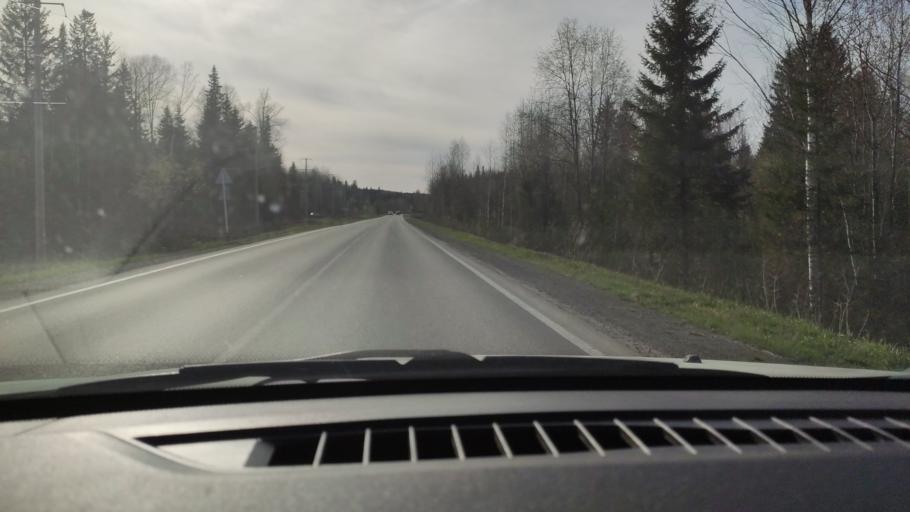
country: RU
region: Perm
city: Novyye Lyady
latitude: 57.9580
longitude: 56.5562
